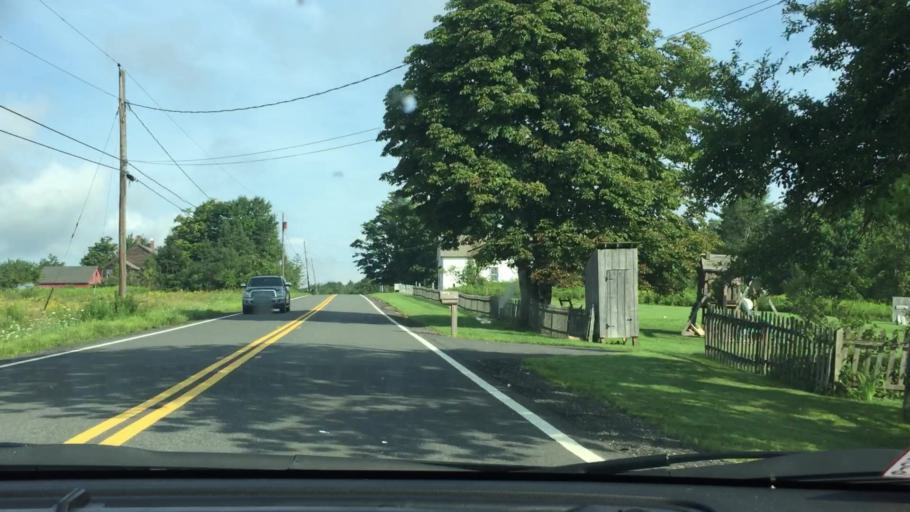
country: US
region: Massachusetts
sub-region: Berkshire County
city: Becket
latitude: 42.3647
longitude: -73.1420
